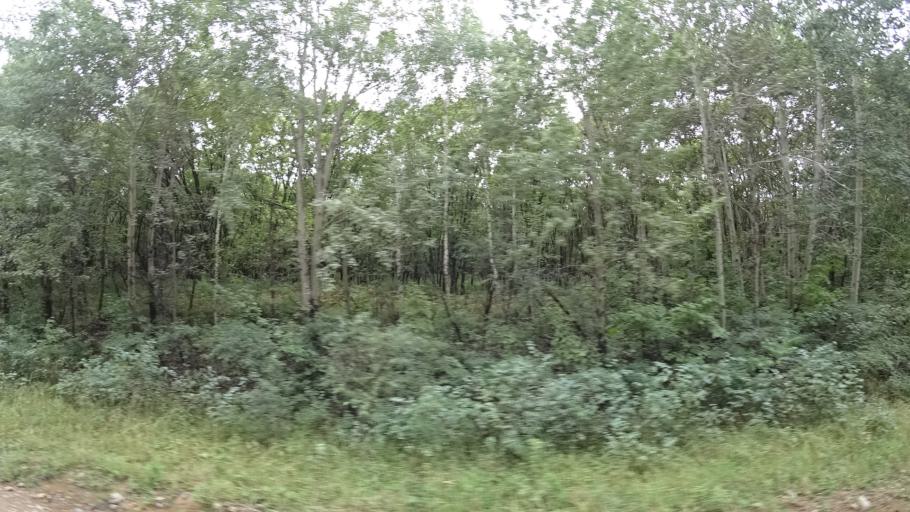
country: RU
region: Primorskiy
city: Lyalichi
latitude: 44.0847
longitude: 132.4428
